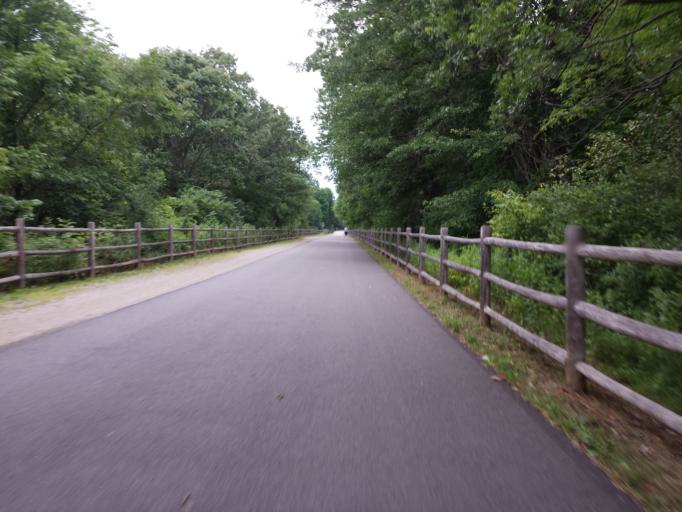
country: US
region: New York
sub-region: Dutchess County
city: Red Oaks Mill
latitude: 41.6385
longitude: -73.8594
